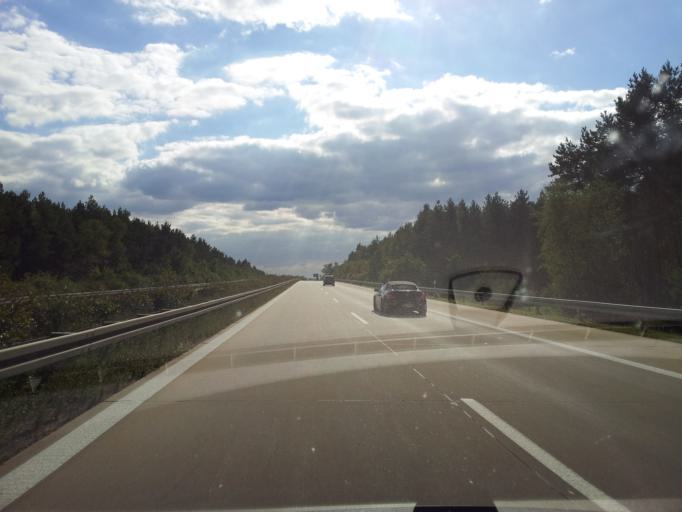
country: DE
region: Brandenburg
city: Schipkau
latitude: 51.5061
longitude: 13.9035
